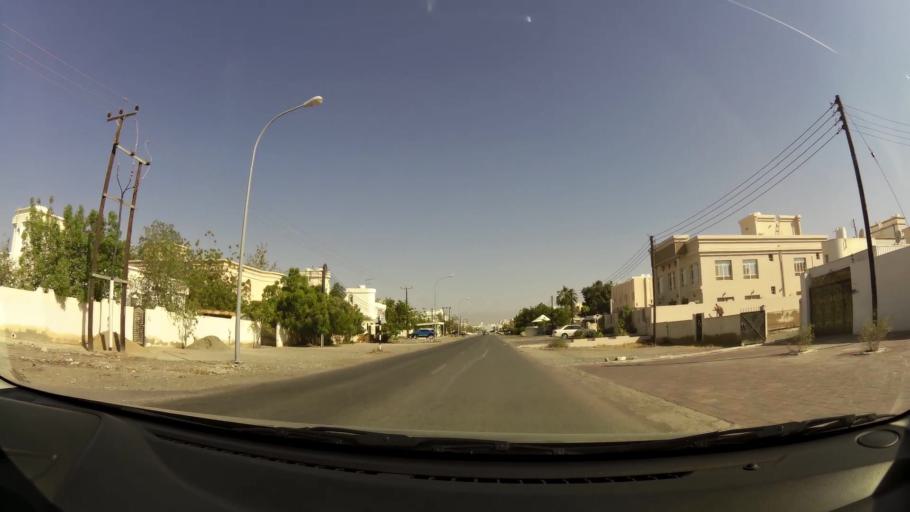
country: OM
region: Muhafazat Masqat
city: As Sib al Jadidah
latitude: 23.6307
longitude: 58.2071
